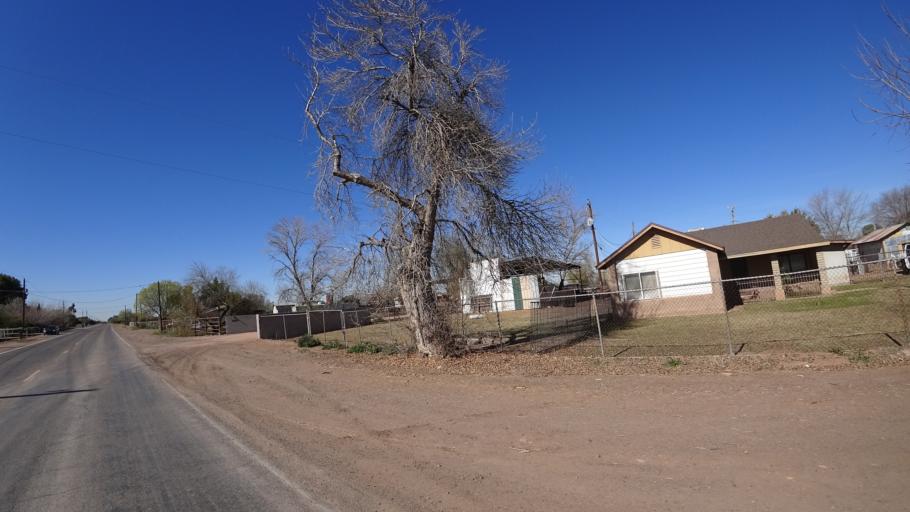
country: US
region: Arizona
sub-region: Maricopa County
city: Tolleson
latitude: 33.3922
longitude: -112.2769
